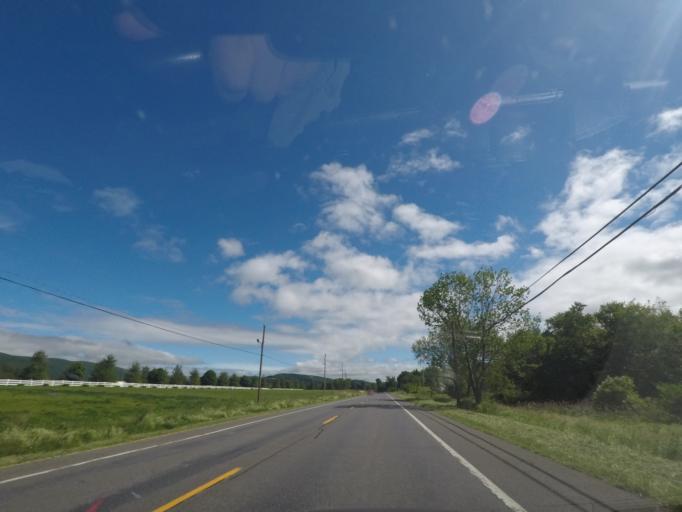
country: US
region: New York
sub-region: Dutchess County
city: Pine Plains
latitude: 42.0868
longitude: -73.5440
